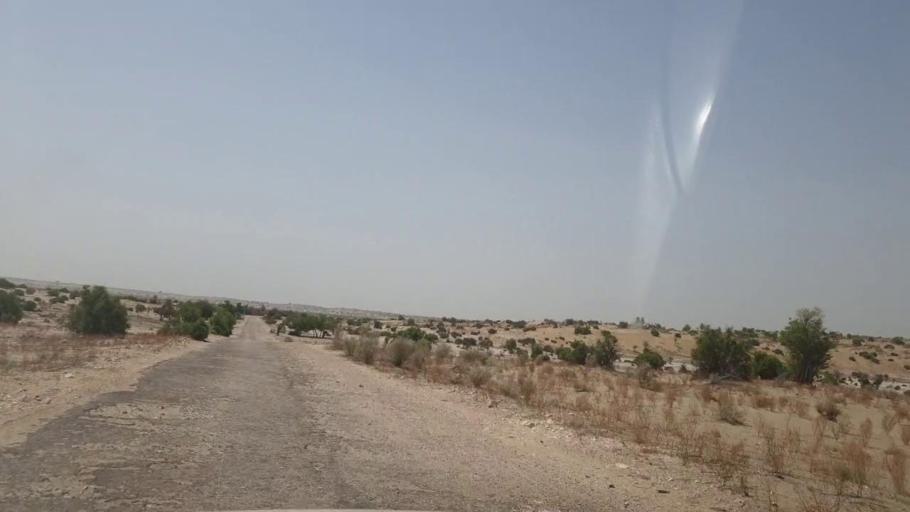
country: PK
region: Sindh
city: Khanpur
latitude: 27.3510
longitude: 69.3180
